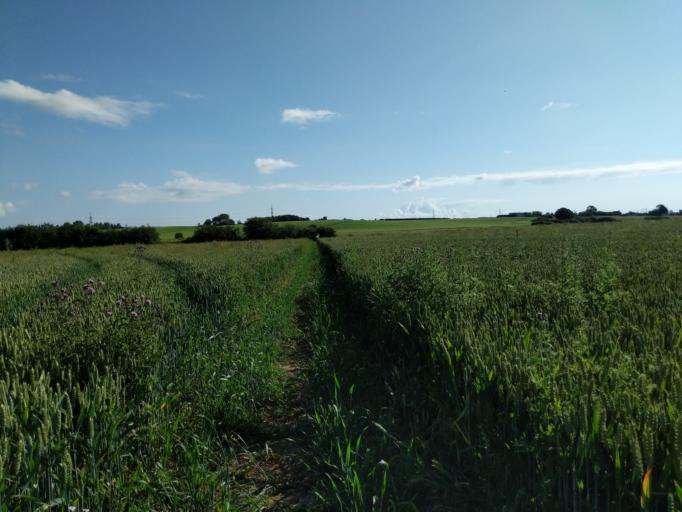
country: GB
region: England
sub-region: Kent
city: Faversham
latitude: 51.3287
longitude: 0.9384
